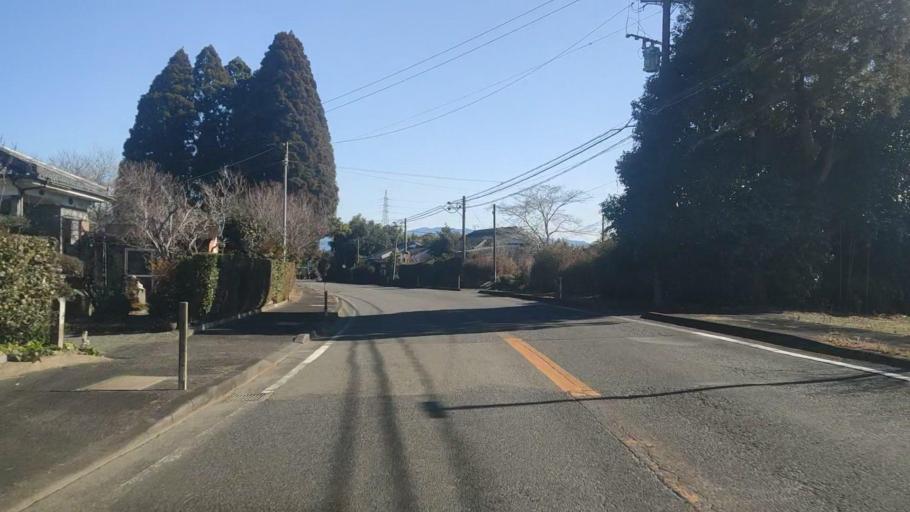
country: JP
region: Kagoshima
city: Sueyoshicho-ninokata
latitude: 31.6953
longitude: 130.9939
